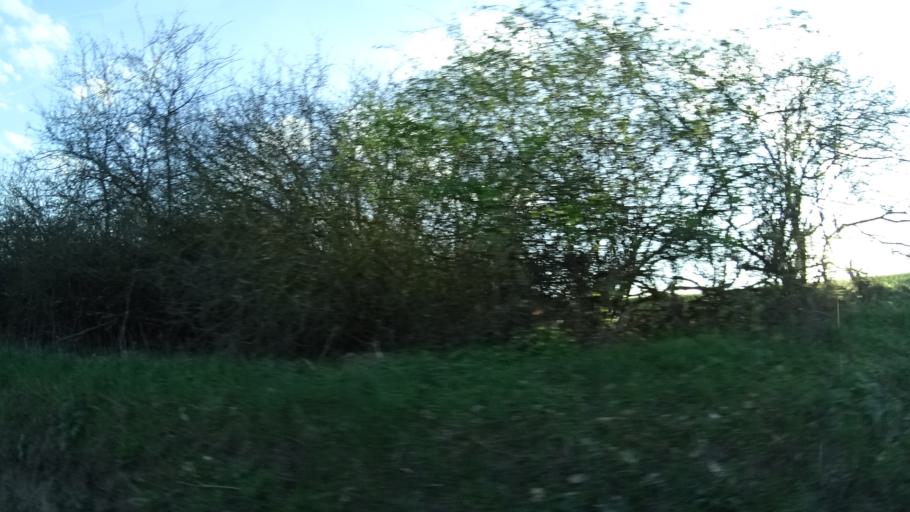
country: DE
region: Rheinland-Pfalz
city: Unkenbach
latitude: 49.7253
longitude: 7.7482
